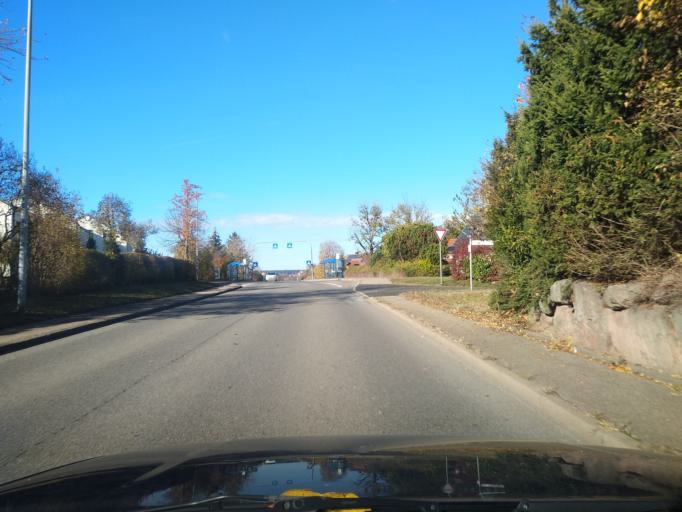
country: DE
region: Baden-Wuerttemberg
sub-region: Karlsruhe Region
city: Bad Liebenzell
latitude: 48.7692
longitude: 8.7522
